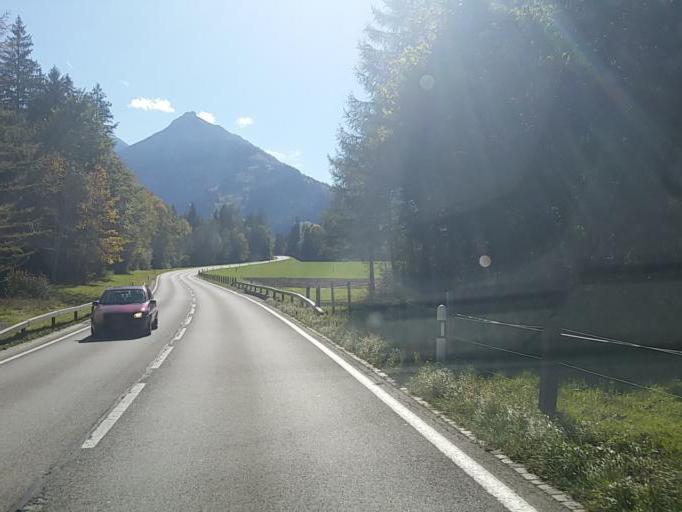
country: CH
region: Bern
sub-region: Frutigen-Niedersimmental District
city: Frutigen
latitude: 46.6010
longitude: 7.6611
